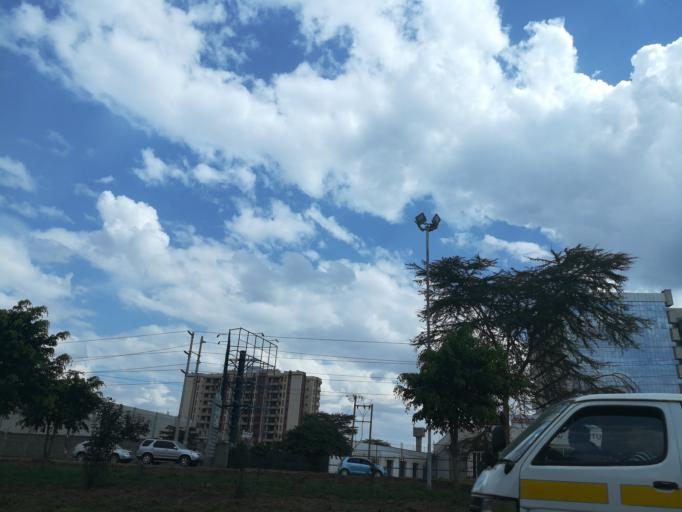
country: KE
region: Nairobi Area
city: Pumwani
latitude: -1.3221
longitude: 36.8429
